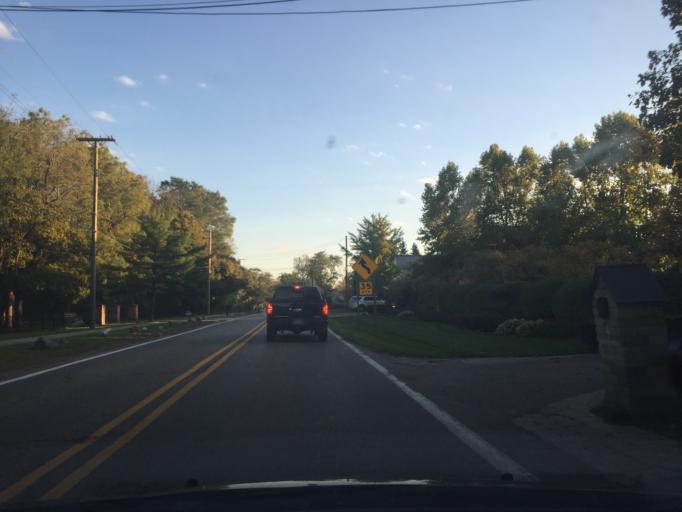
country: US
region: Michigan
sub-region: Oakland County
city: Bloomfield Hills
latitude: 42.5883
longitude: -83.2868
